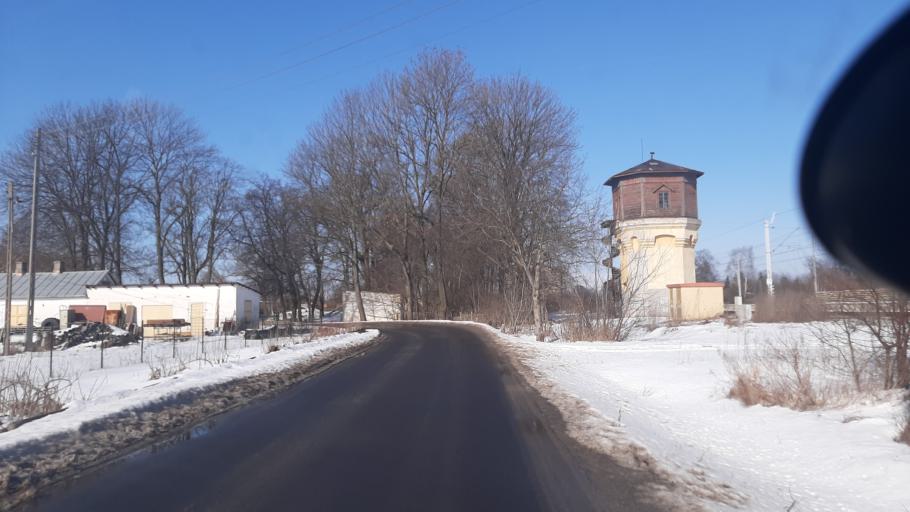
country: PL
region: Lublin Voivodeship
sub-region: Powiat lubelski
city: Wojciechow
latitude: 51.2845
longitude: 22.2866
